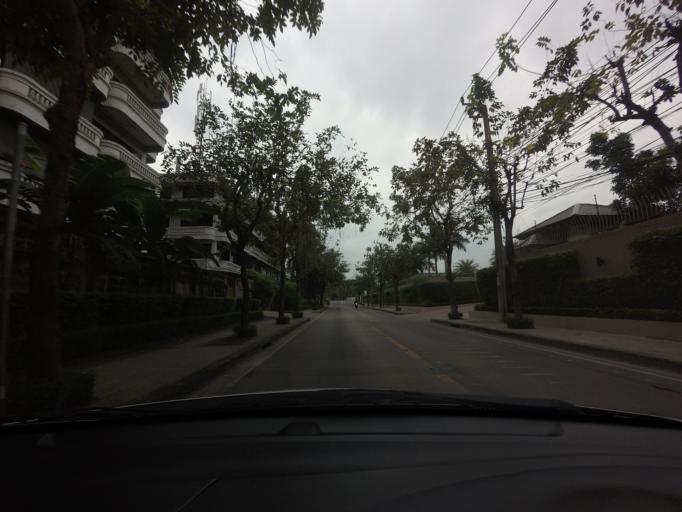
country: TH
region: Bangkok
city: Chom Thong
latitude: 13.6721
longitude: 100.4652
